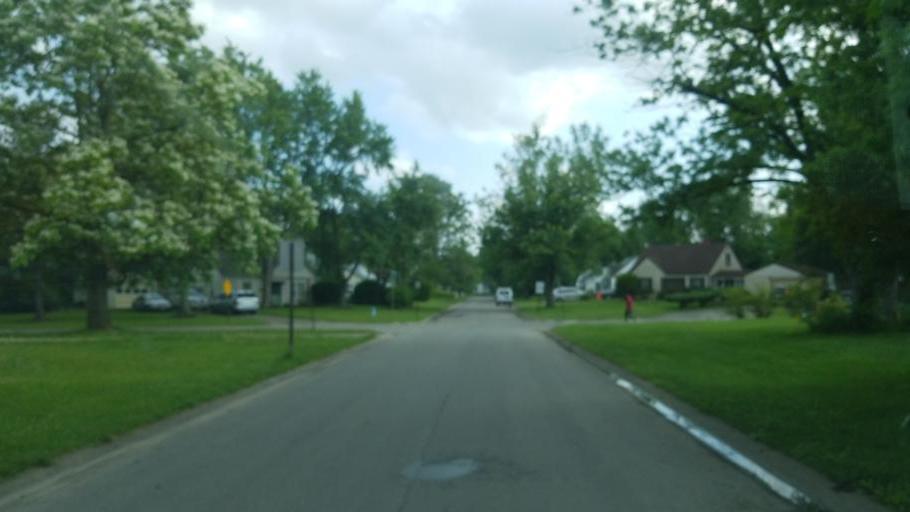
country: US
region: Ohio
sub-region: Franklin County
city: Minerva Park
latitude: 40.0294
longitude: -82.9506
